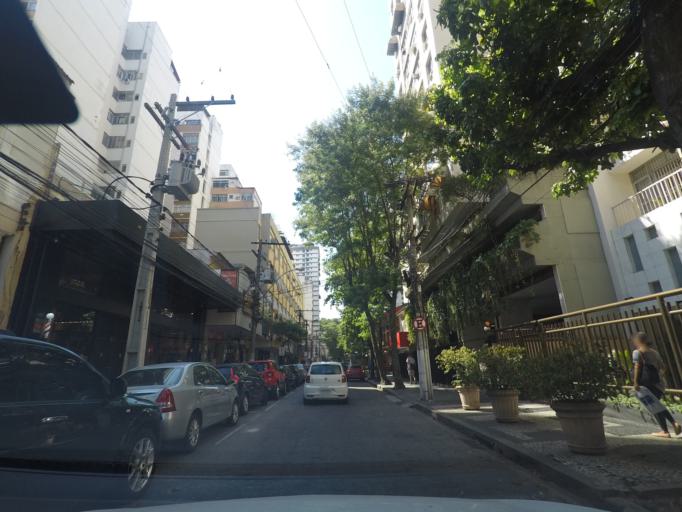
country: BR
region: Rio de Janeiro
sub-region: Niteroi
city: Niteroi
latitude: -22.9034
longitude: -43.1125
